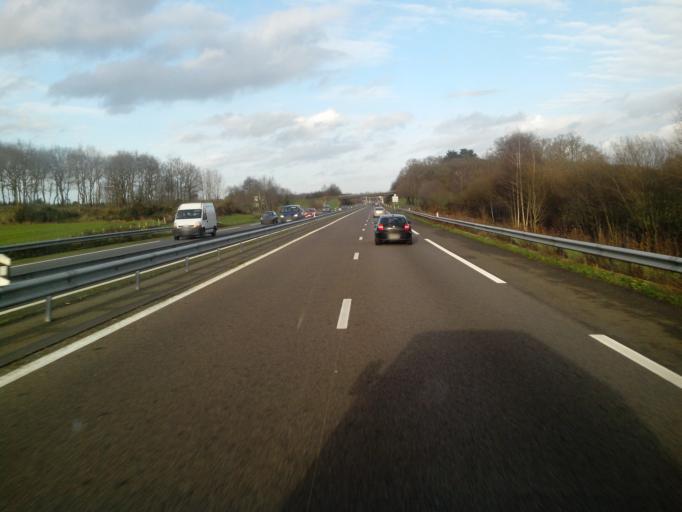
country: FR
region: Brittany
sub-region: Departement d'Ille-et-Vilaine
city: Saint-Pierre-de-Plesguen
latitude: 48.4504
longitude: -1.9230
